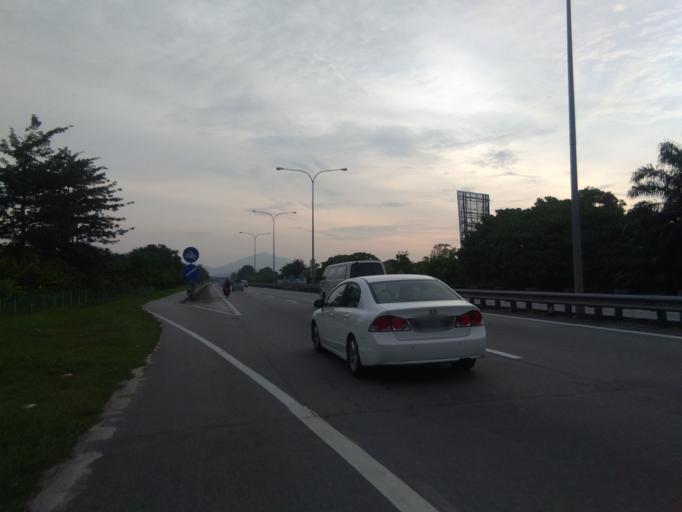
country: MY
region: Kedah
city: Kulim
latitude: 5.4306
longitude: 100.5490
